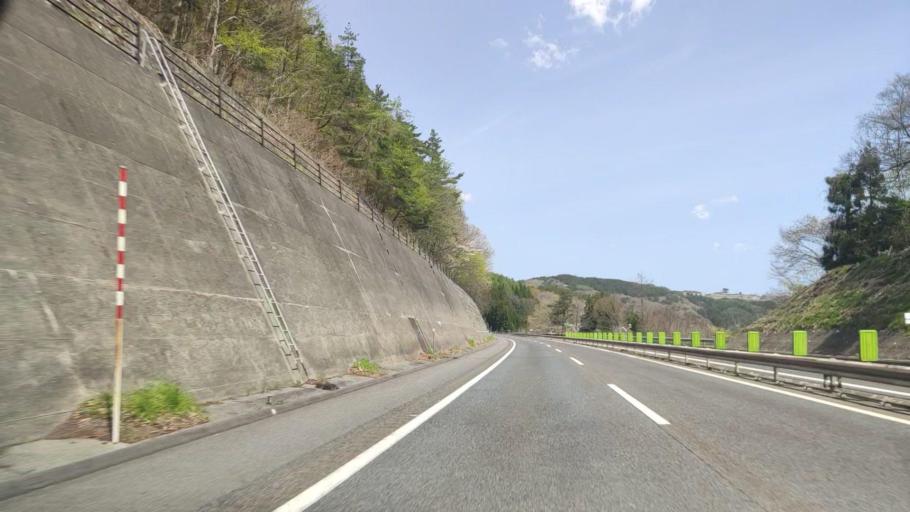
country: JP
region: Aomori
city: Hachinohe
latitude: 40.3566
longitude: 141.4499
